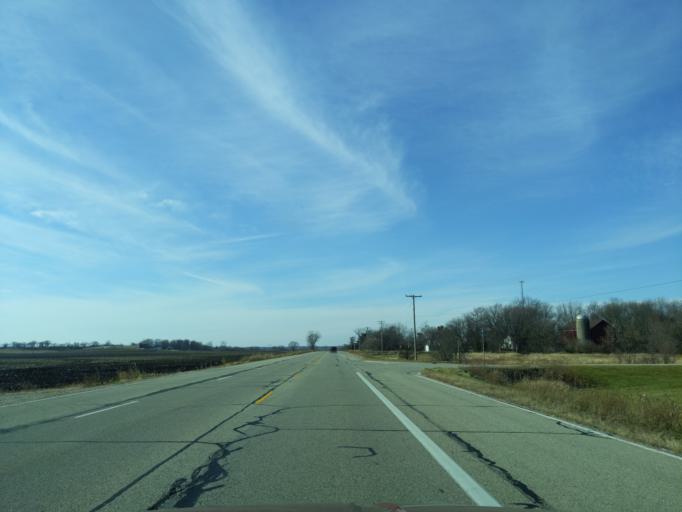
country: US
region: Wisconsin
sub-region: Walworth County
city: Whitewater
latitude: 42.8075
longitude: -88.6696
